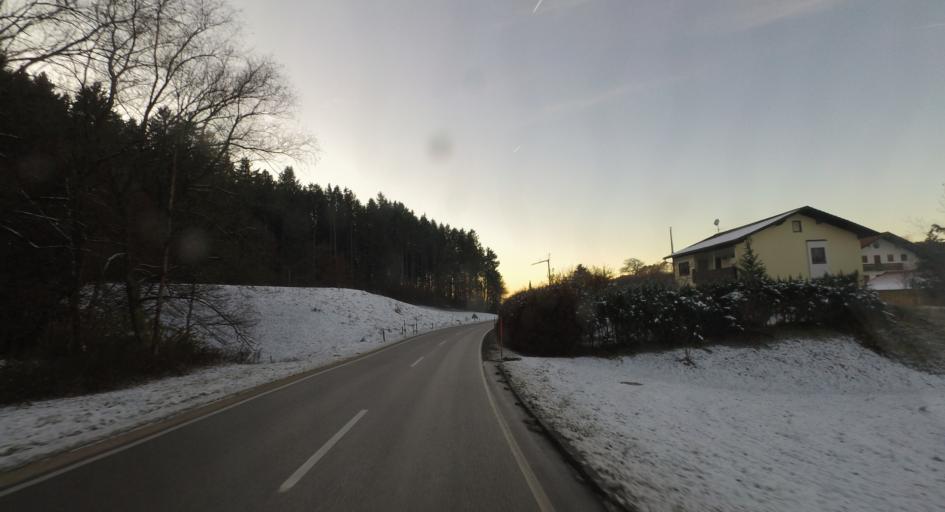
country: DE
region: Bavaria
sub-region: Upper Bavaria
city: Nussdorf
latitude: 47.8868
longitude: 12.5937
